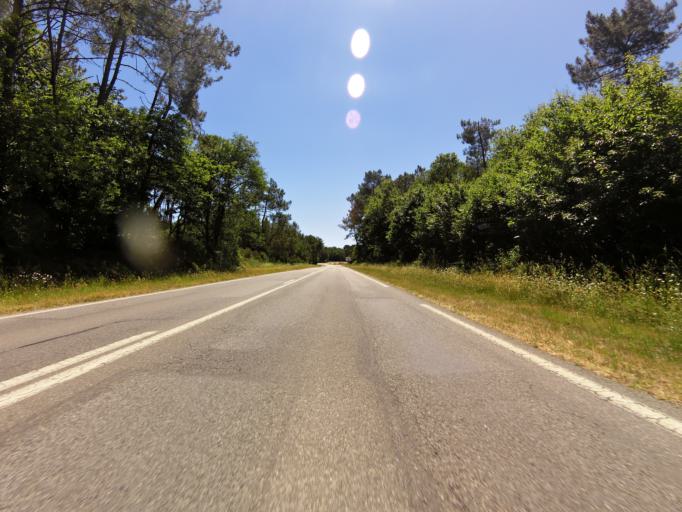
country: FR
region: Brittany
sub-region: Departement du Morbihan
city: Ferel
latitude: 47.4864
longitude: -2.3869
